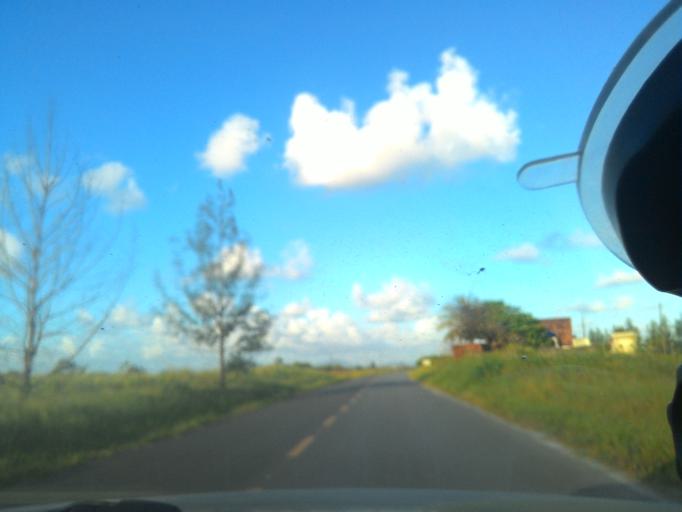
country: BR
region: Sao Paulo
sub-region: Iguape
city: Iguape
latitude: -24.8252
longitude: -47.6637
